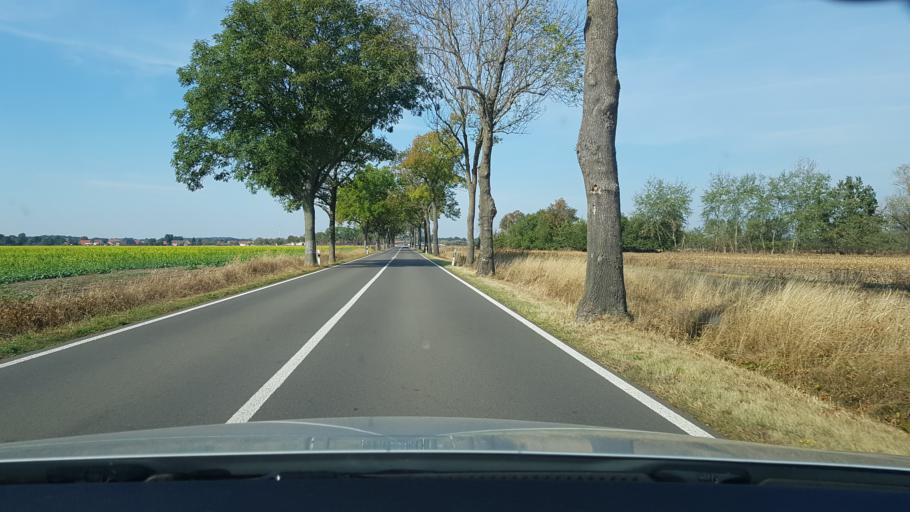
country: DE
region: Brandenburg
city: Mixdorf
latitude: 52.1695
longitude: 14.3481
